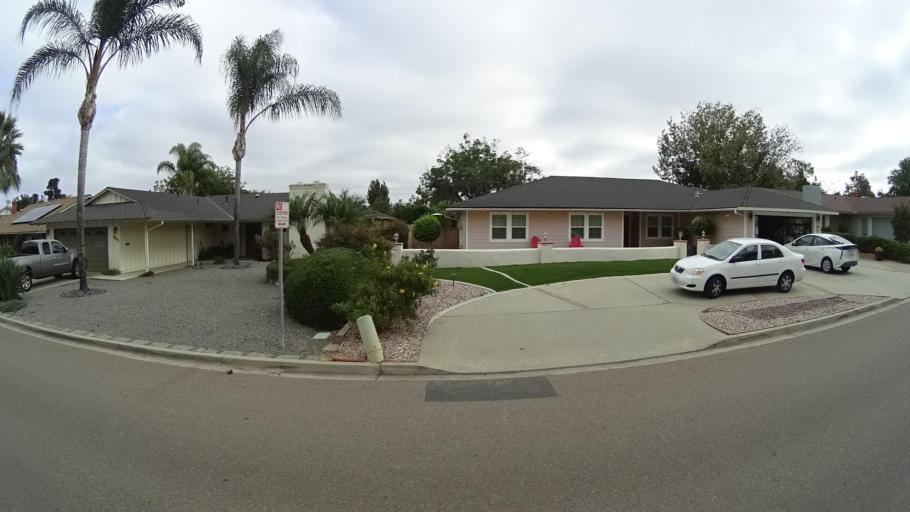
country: US
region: California
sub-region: San Diego County
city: Lake San Marcos
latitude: 33.1282
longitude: -117.2000
